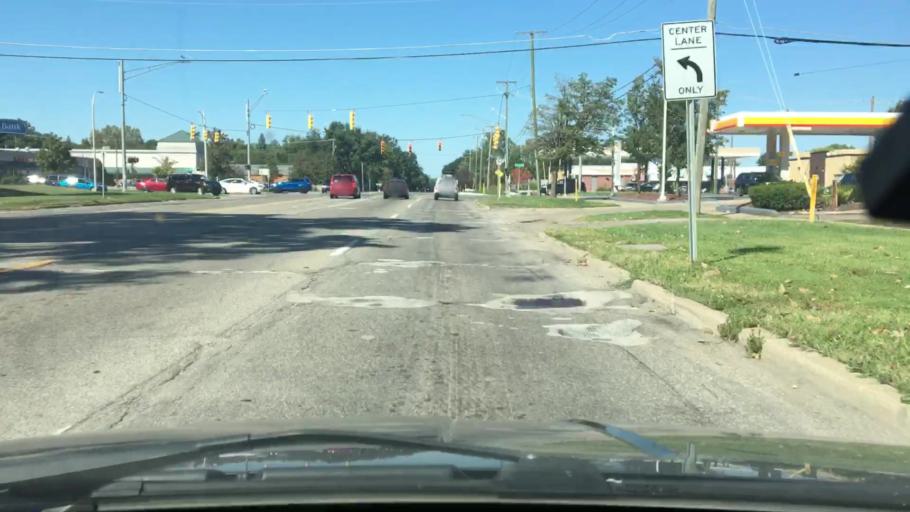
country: US
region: Michigan
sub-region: Wayne County
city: Livonia
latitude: 42.3969
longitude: -83.3539
